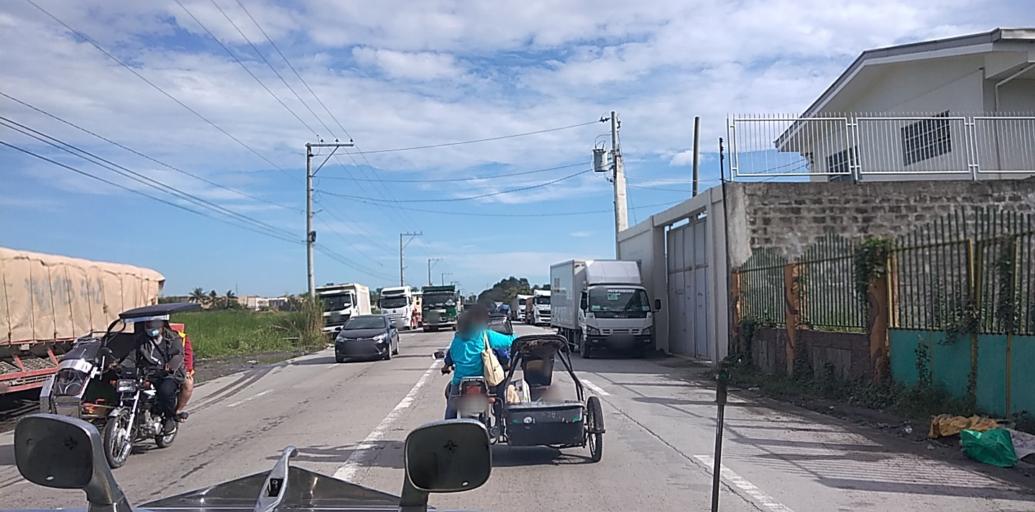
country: PH
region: Central Luzon
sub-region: Province of Pampanga
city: Bulaon
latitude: 15.1026
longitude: 120.6588
